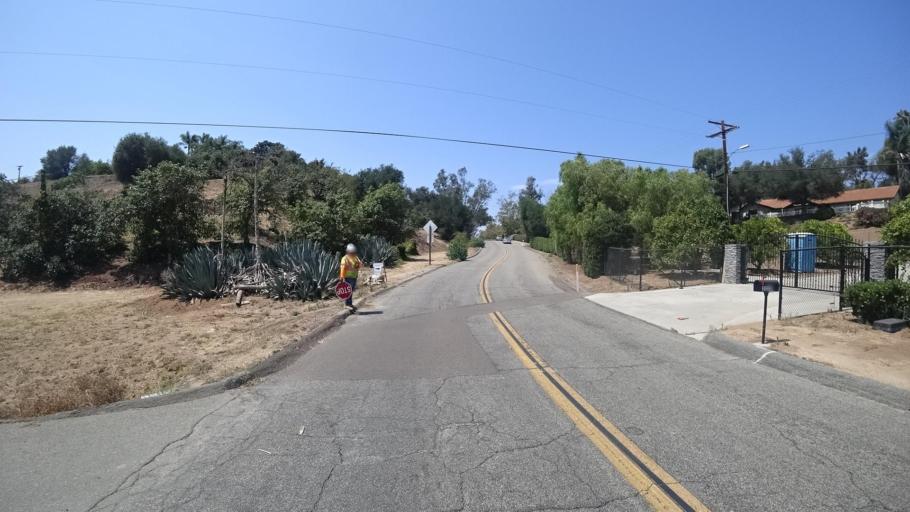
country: US
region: California
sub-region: San Diego County
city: Bonsall
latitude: 33.3133
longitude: -117.2100
